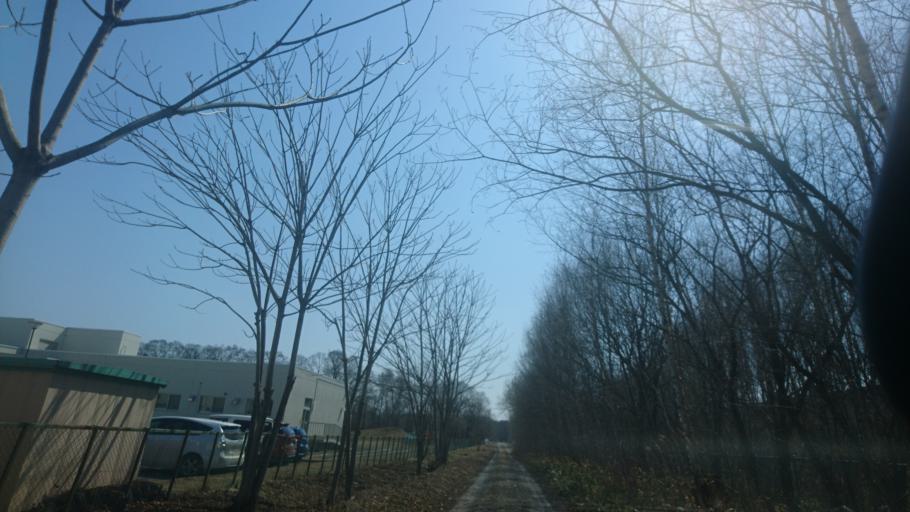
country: JP
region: Hokkaido
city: Obihiro
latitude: 42.9172
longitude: 143.1105
